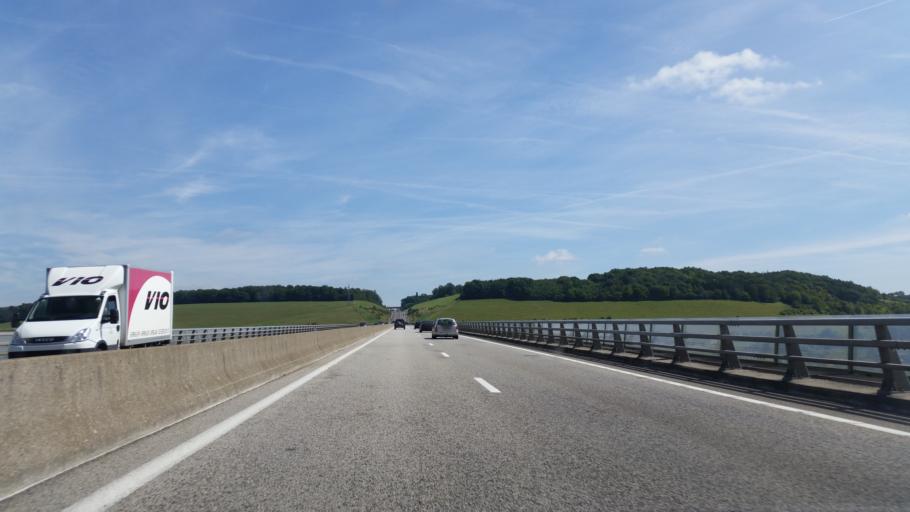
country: FR
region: Haute-Normandie
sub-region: Departement de la Seine-Maritime
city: Aumale
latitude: 49.7819
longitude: 1.7508
